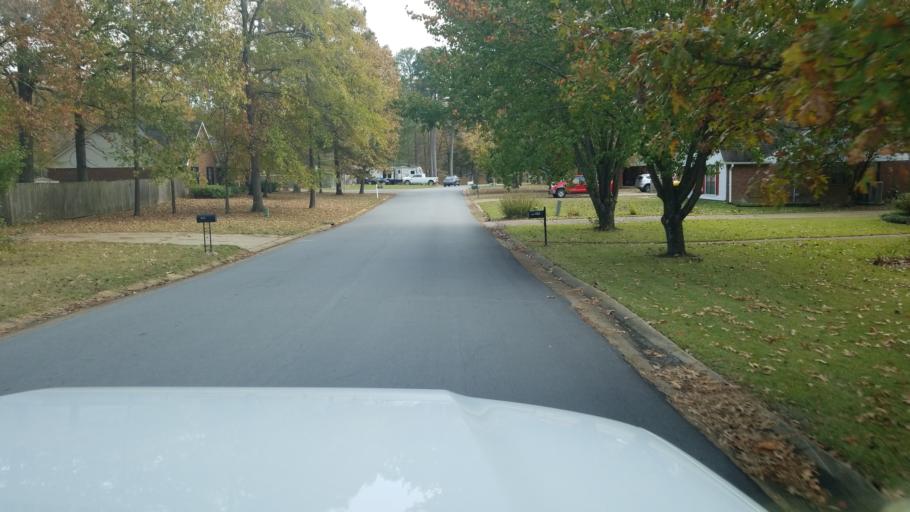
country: US
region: Mississippi
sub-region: Madison County
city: Ridgeland
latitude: 32.3869
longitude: -90.0347
